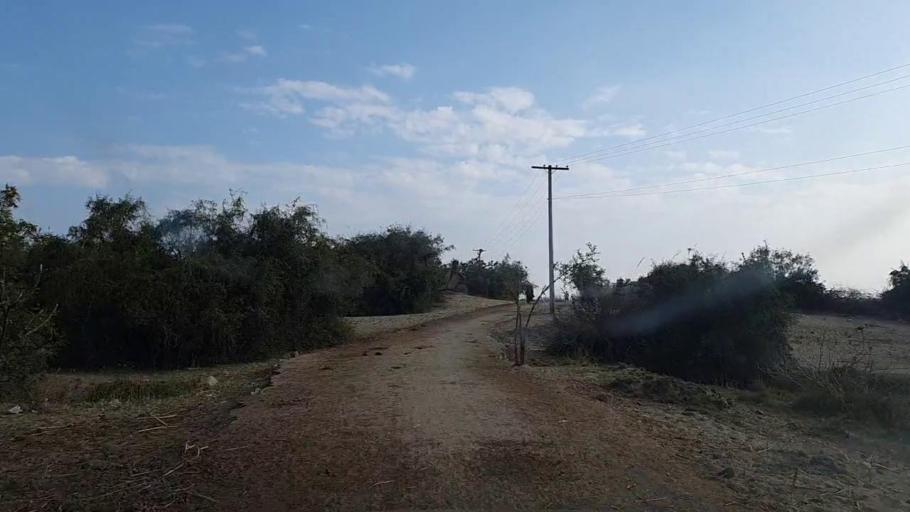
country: PK
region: Sindh
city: Sanghar
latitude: 26.2022
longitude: 69.0274
